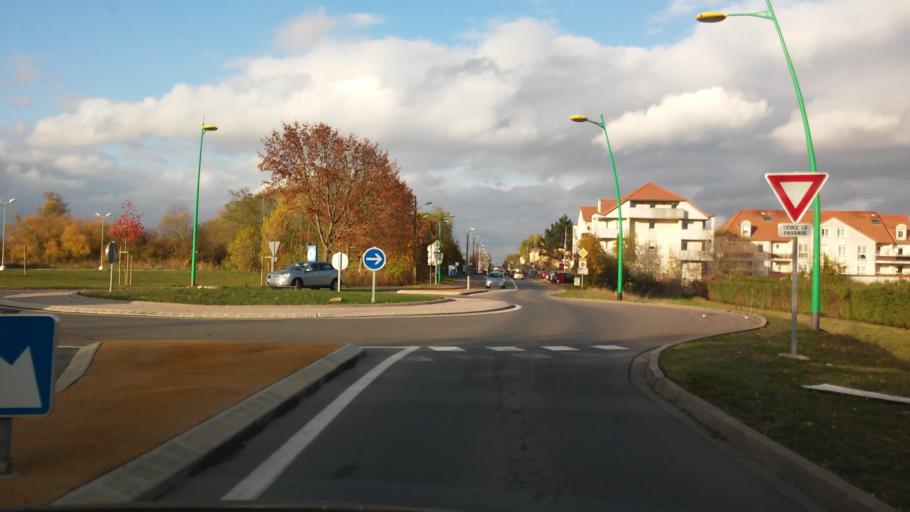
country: FR
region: Lorraine
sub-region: Departement de la Moselle
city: Talange
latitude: 49.2260
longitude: 6.1668
